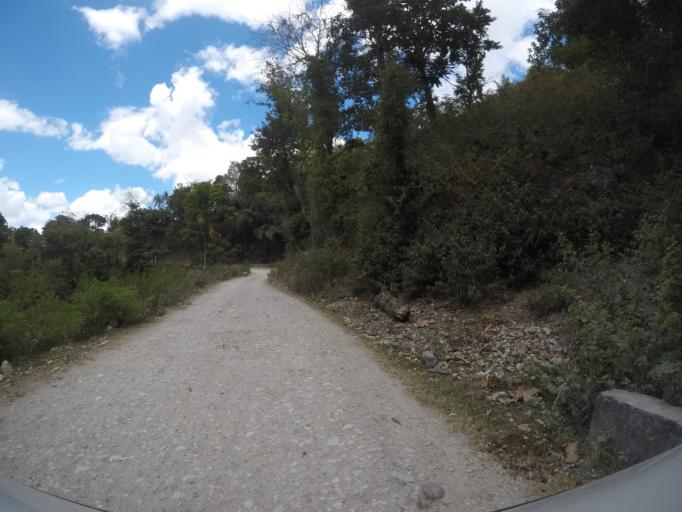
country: TL
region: Baucau
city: Baucau
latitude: -8.5275
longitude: 126.6927
